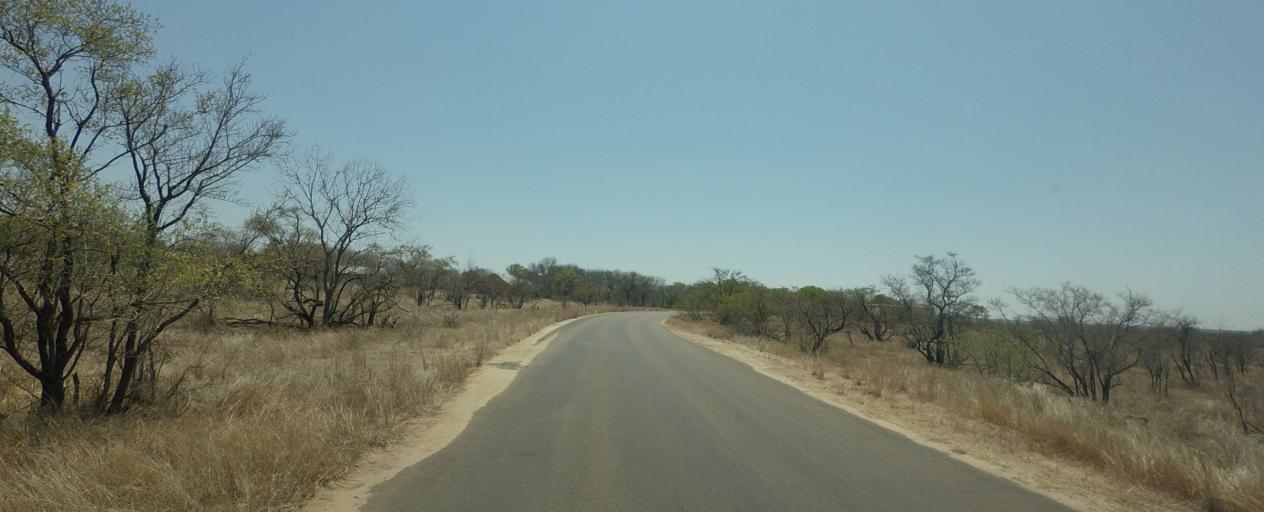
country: ZA
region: Limpopo
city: Thulamahashi
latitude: -24.4778
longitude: 31.3907
